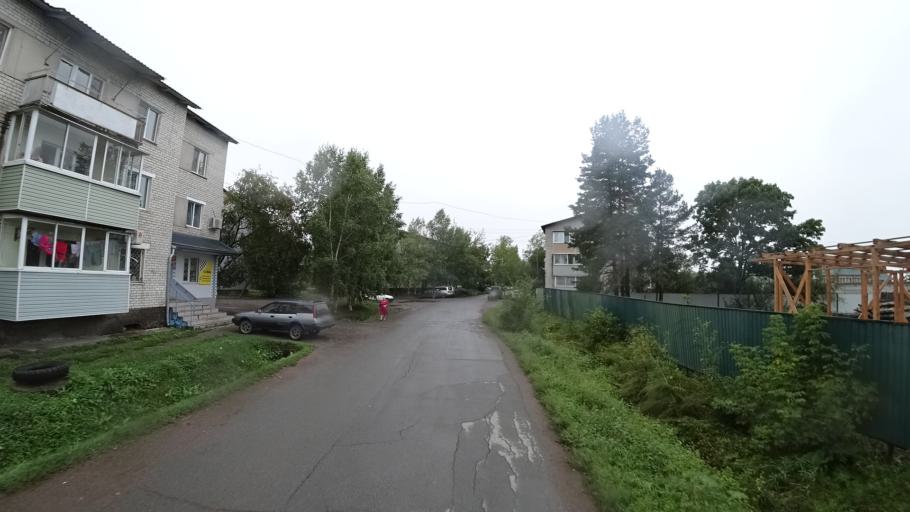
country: RU
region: Primorskiy
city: Monastyrishche
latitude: 44.1946
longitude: 132.4239
